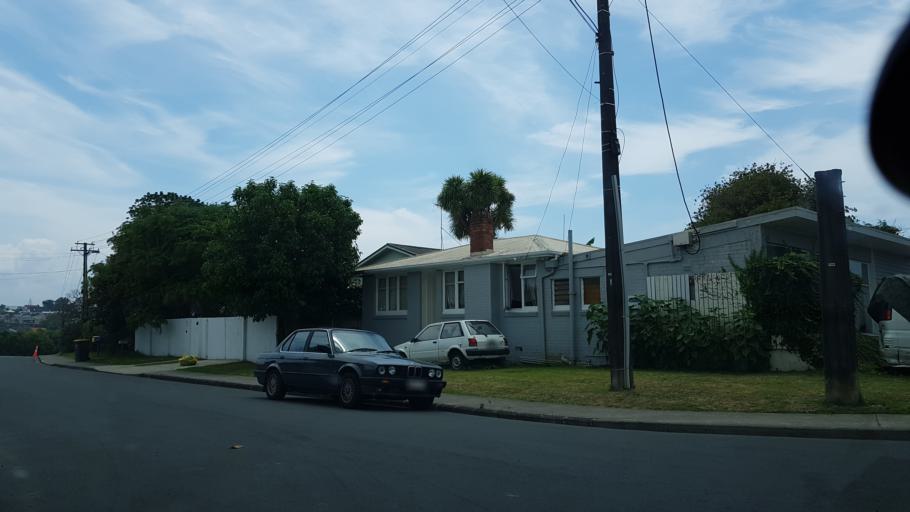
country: NZ
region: Auckland
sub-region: Auckland
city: North Shore
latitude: -36.8044
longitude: 174.7832
